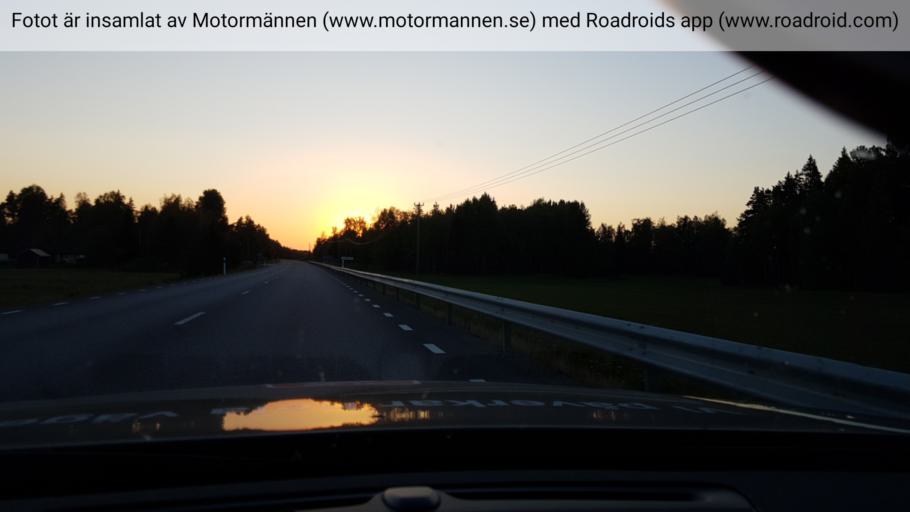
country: SE
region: Uppsala
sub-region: Osthammars Kommun
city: Bjorklinge
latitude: 59.9685
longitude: 17.3757
